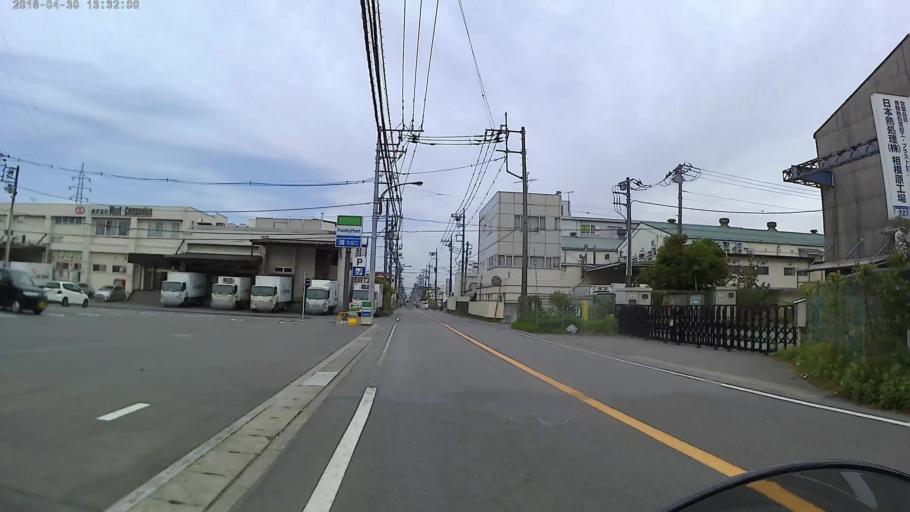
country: JP
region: Tokyo
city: Hachioji
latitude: 35.5906
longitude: 139.3301
